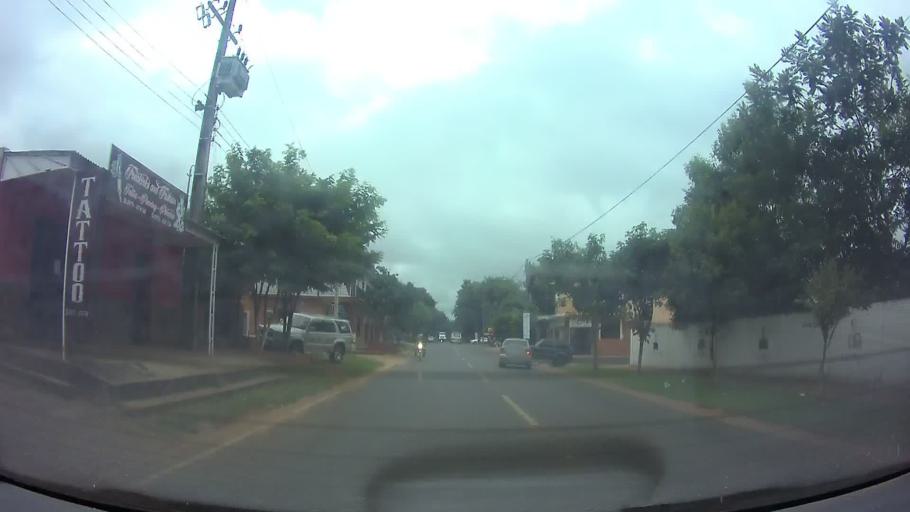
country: PY
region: Paraguari
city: Carapegua
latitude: -25.7671
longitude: -57.2475
